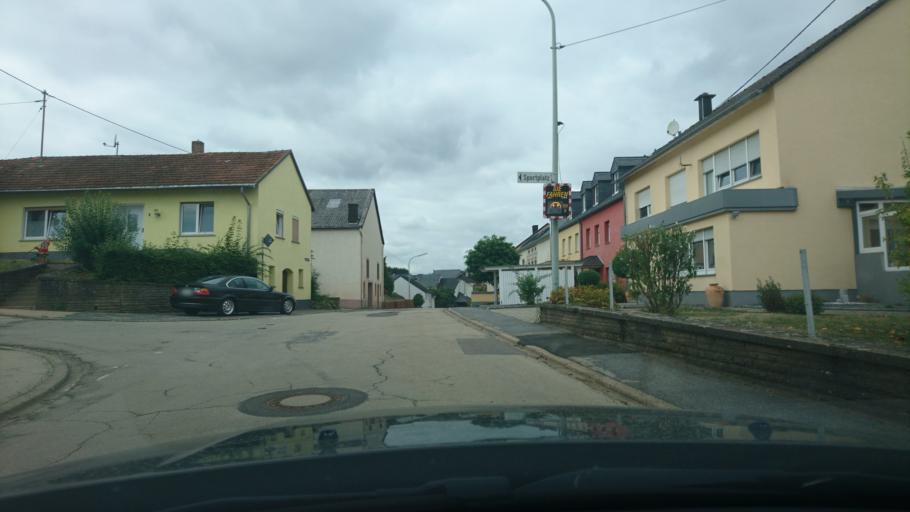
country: DE
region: Rheinland-Pfalz
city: Wiltingen
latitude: 49.6806
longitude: 6.6080
